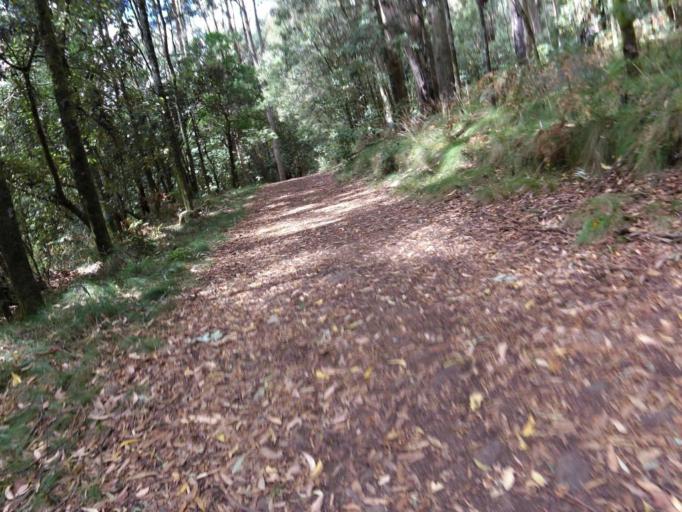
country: AU
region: Victoria
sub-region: Hume
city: Sunbury
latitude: -37.3689
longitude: 144.5845
